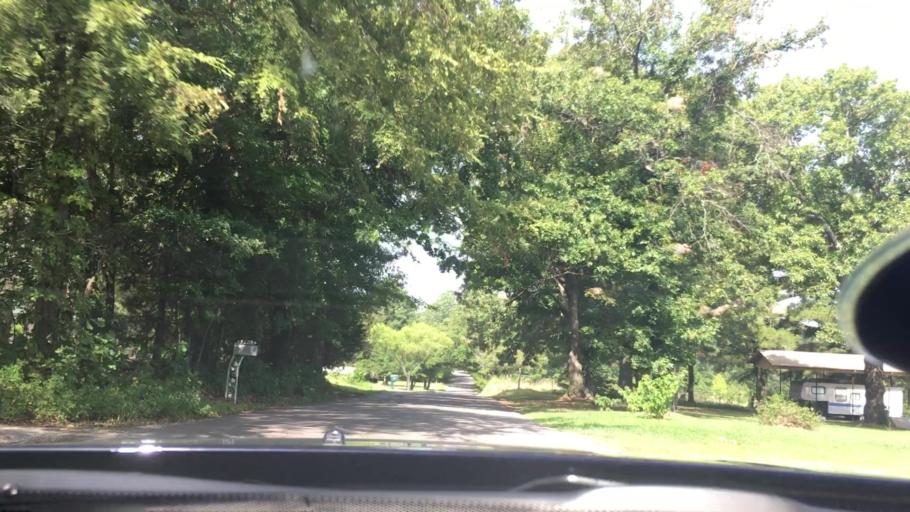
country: US
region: Oklahoma
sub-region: Atoka County
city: Atoka
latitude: 34.3603
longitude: -96.1582
